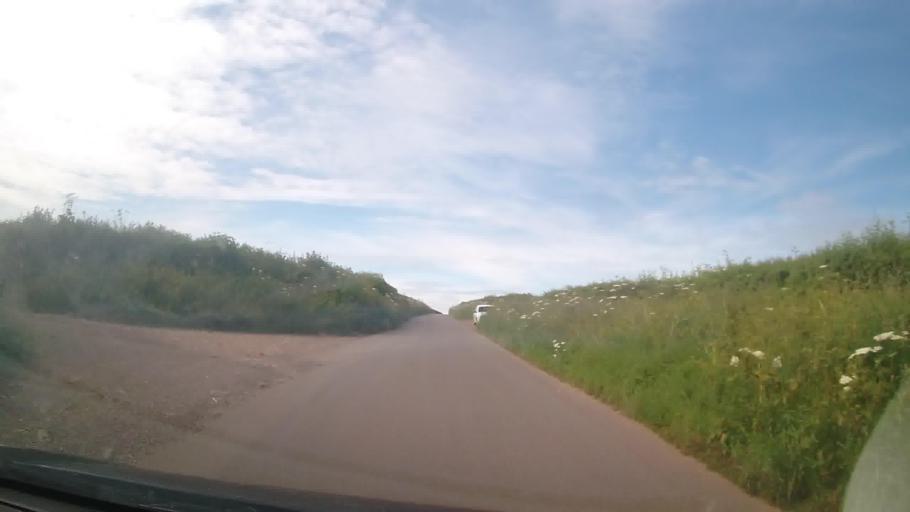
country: GB
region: England
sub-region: Devon
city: Salcombe
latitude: 50.2448
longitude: -3.6808
